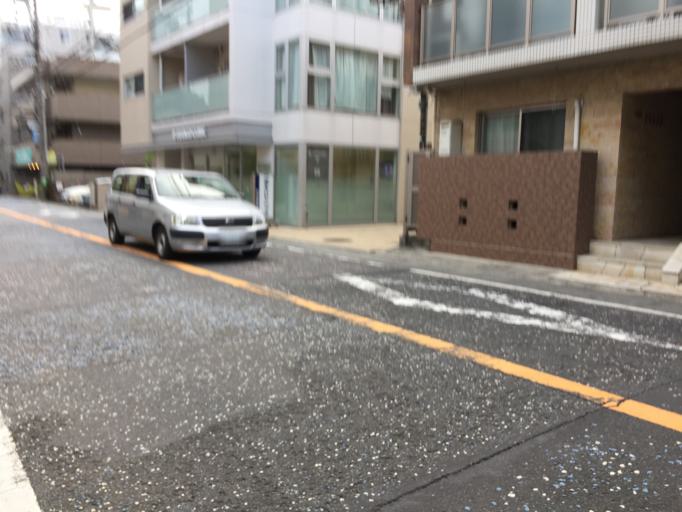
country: JP
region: Tokyo
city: Chofugaoka
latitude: 35.6061
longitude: 139.6189
